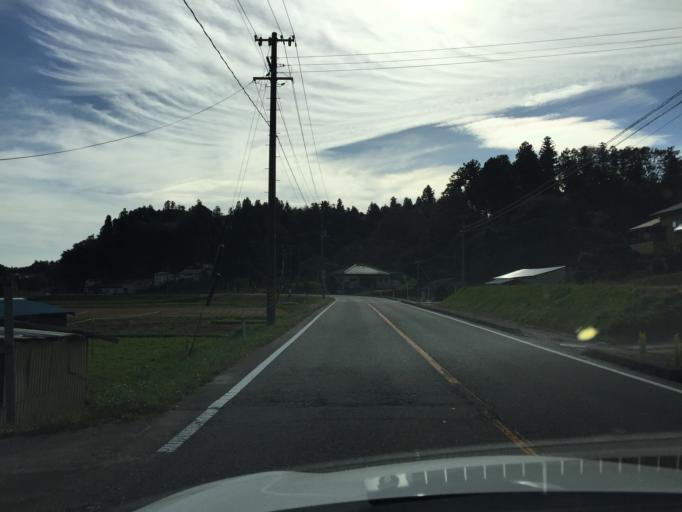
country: JP
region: Fukushima
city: Miharu
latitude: 37.4076
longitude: 140.4576
